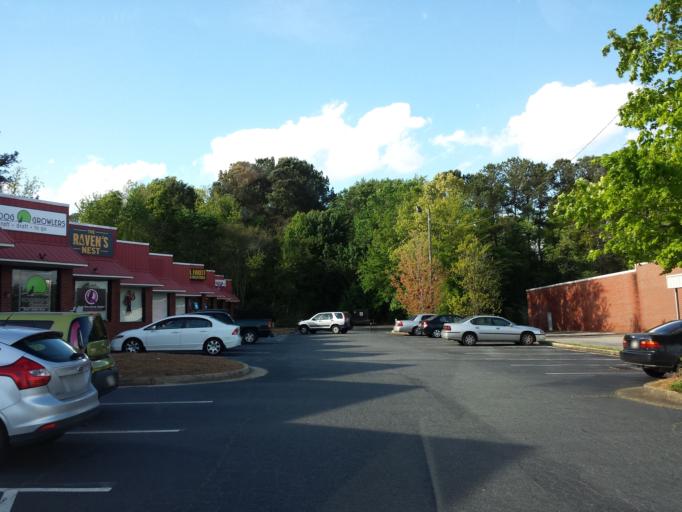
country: US
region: Georgia
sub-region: Cobb County
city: Marietta
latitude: 33.9524
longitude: -84.5726
